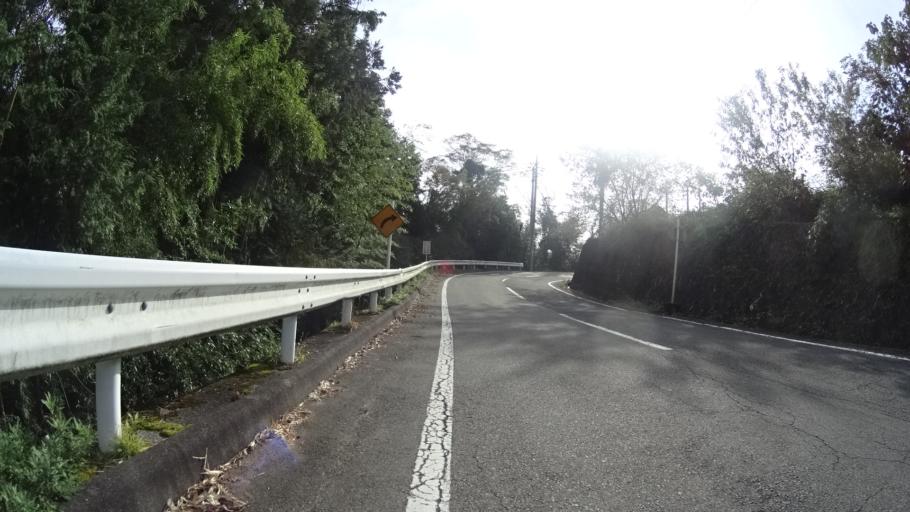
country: JP
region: Yamanashi
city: Uenohara
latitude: 35.6296
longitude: 139.0426
